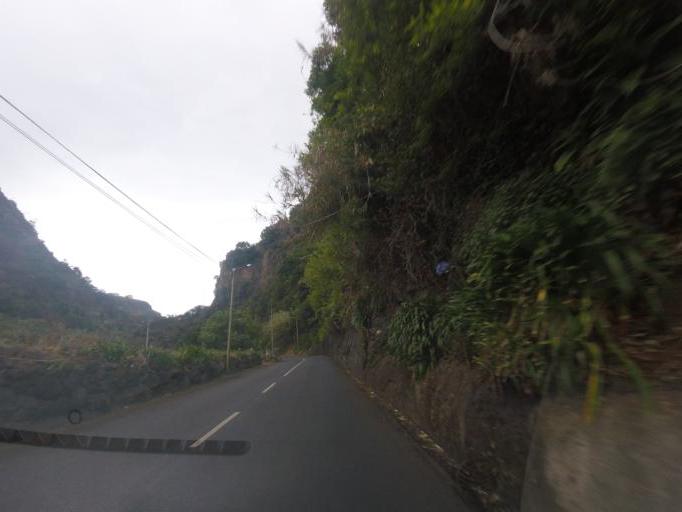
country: PT
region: Madeira
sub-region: Santana
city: Santana
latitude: 32.8170
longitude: -16.8986
